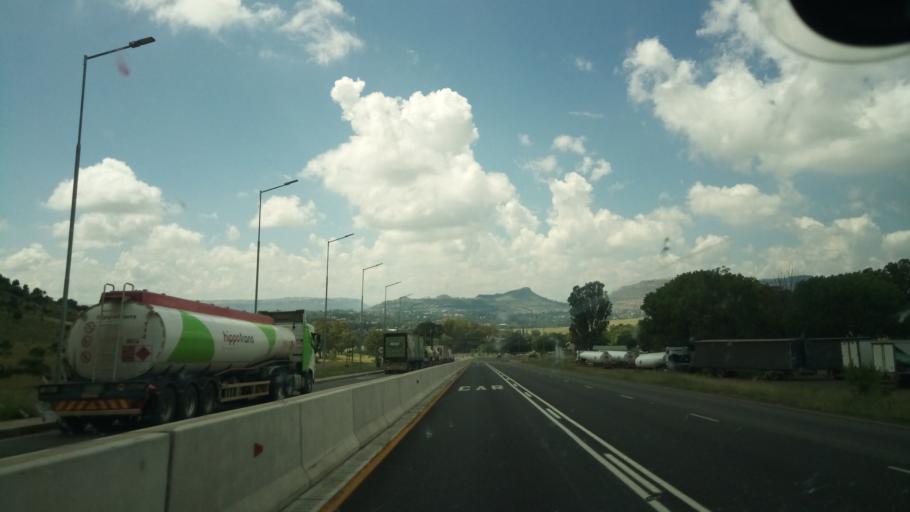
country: LS
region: Maseru
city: Maseru
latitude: -29.2957
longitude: 27.4438
